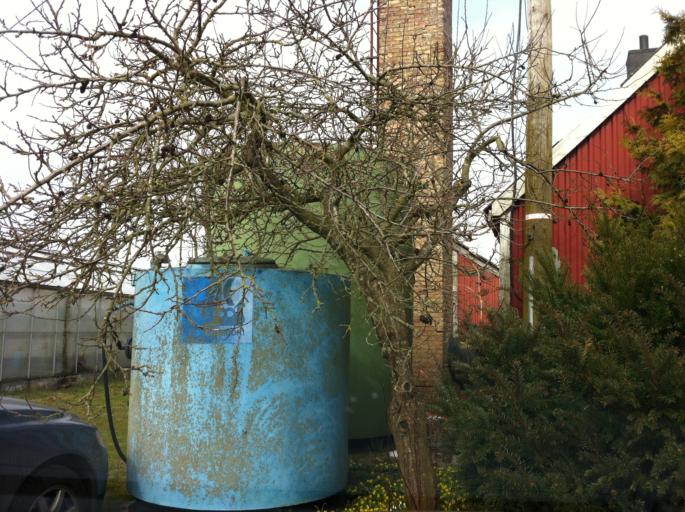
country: SE
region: Skane
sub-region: Svalovs Kommun
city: Teckomatorp
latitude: 55.8404
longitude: 13.0902
